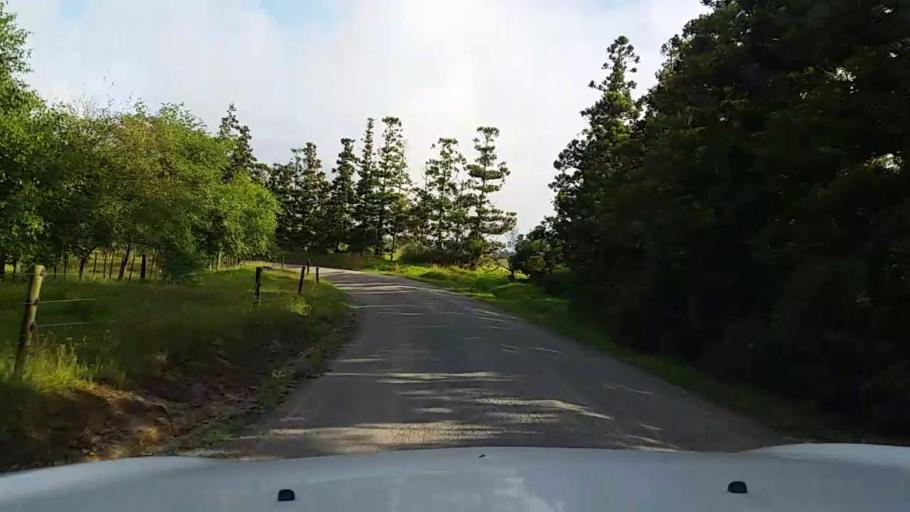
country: NZ
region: Northland
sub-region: Whangarei
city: Maungatapere
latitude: -35.6789
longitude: 174.1786
